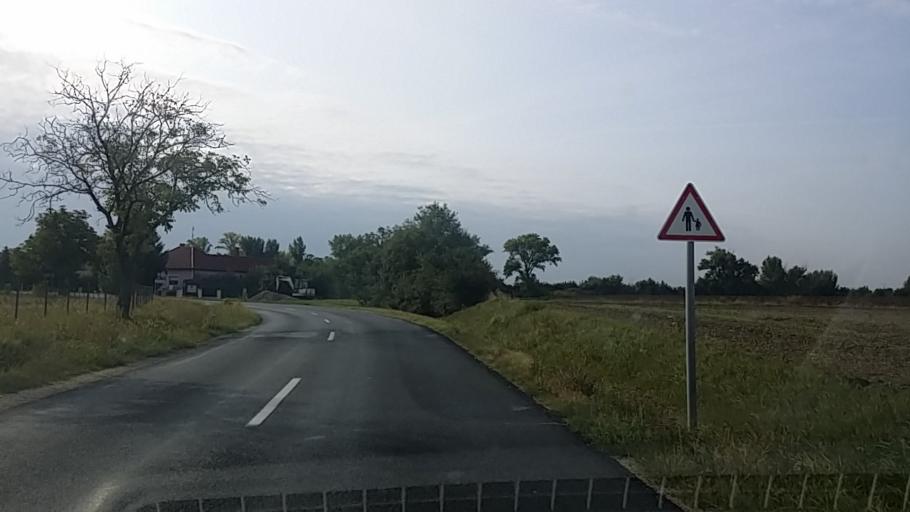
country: HU
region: Gyor-Moson-Sopron
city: Fertoszentmiklos
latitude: 47.6081
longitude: 16.9009
